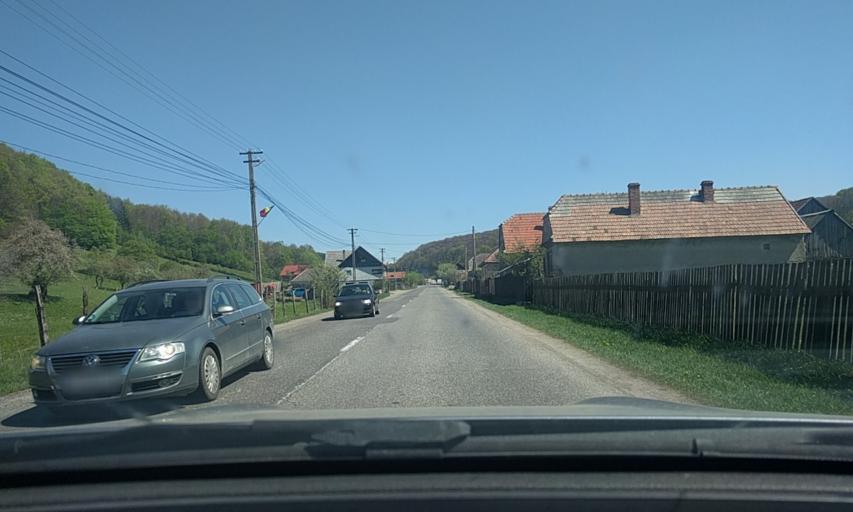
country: RO
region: Covasna
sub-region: Comuna Dobarlau
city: Dobarlau
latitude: 45.6817
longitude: 25.9173
